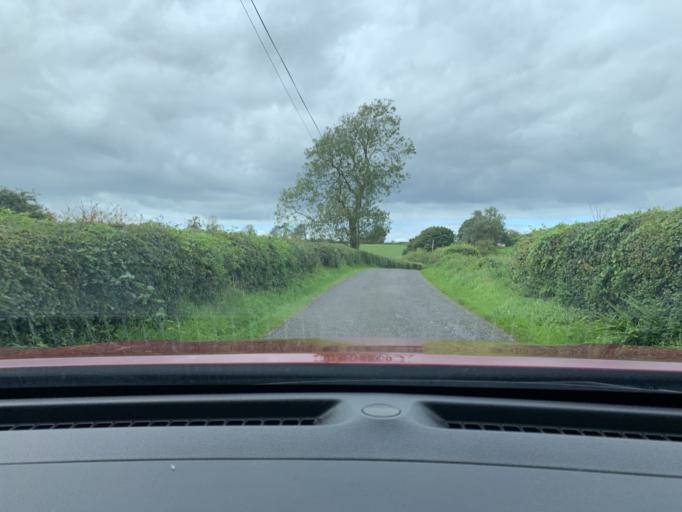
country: IE
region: Connaught
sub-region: Sligo
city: Collooney
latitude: 54.1527
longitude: -8.4273
